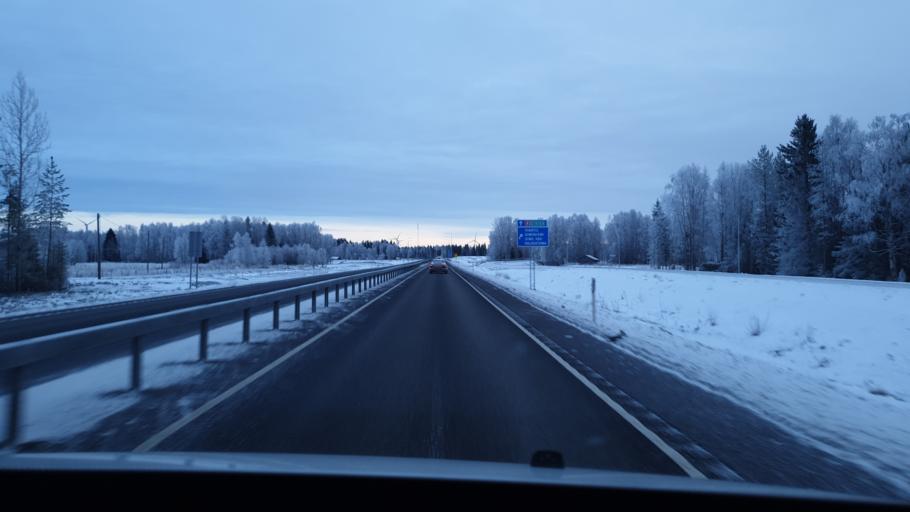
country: FI
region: Lapland
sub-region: Kemi-Tornio
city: Simo
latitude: 65.6712
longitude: 24.9178
